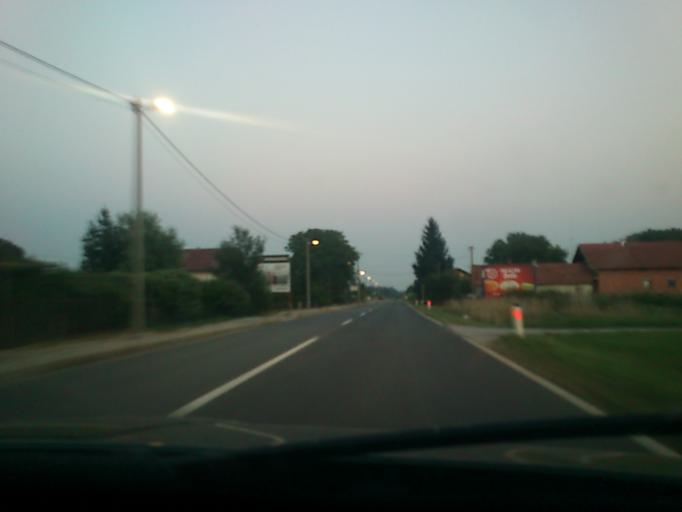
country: SI
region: Starse
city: Starse
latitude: 46.4763
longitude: 15.7476
